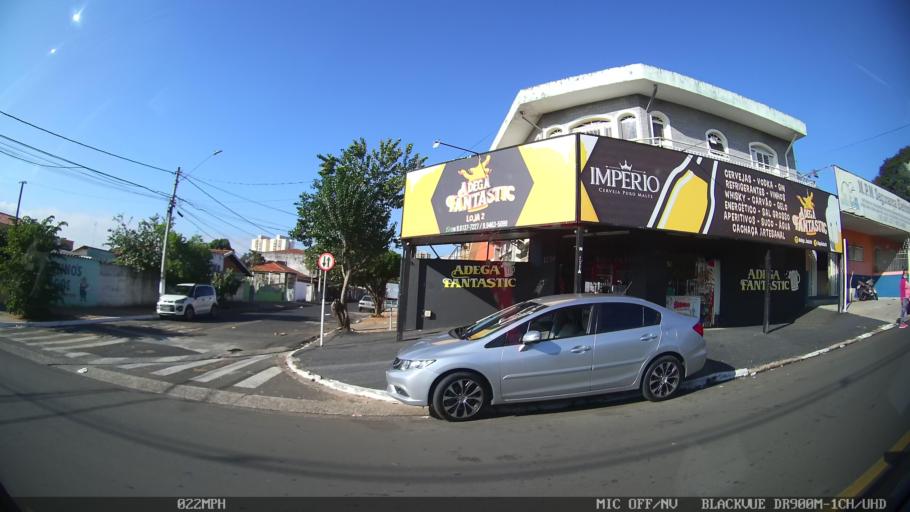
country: BR
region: Sao Paulo
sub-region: Hortolandia
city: Hortolandia
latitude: -22.8985
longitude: -47.1722
